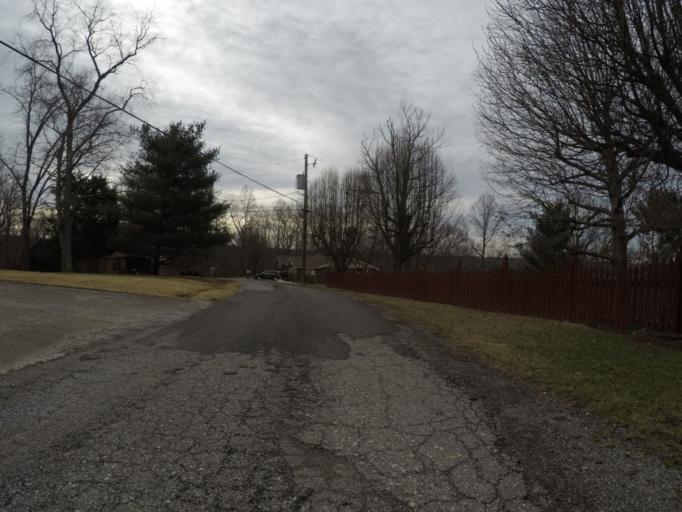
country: US
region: Ohio
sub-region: Lawrence County
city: Burlington
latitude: 38.3781
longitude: -82.5120
